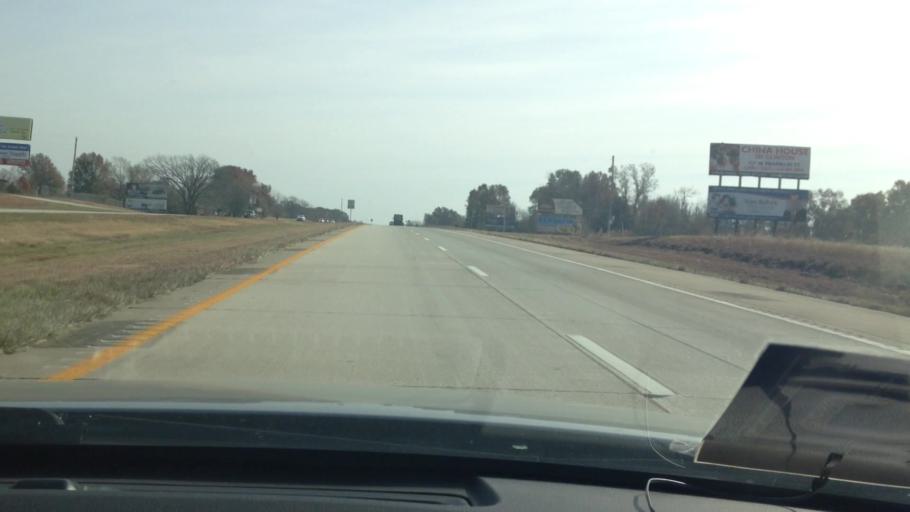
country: US
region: Missouri
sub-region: Henry County
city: Clinton
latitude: 38.4233
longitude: -93.8753
